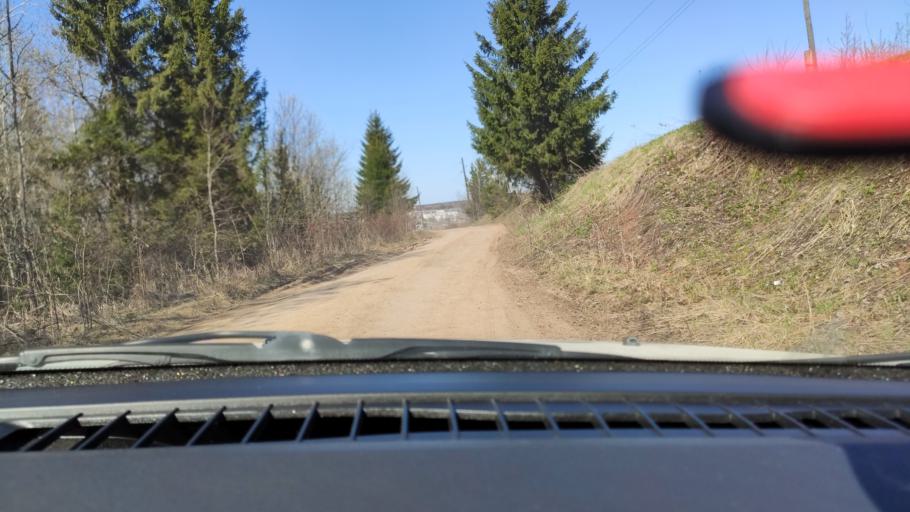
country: RU
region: Perm
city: Bershet'
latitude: 57.7238
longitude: 56.3951
